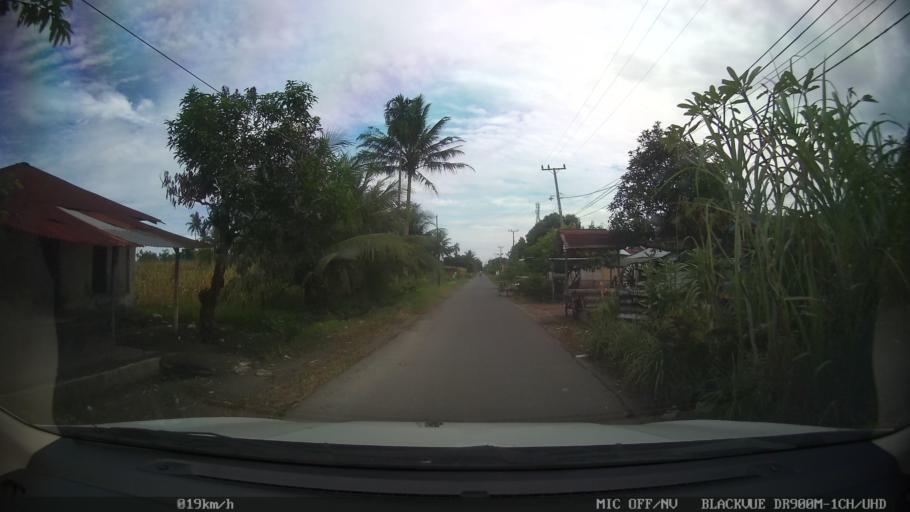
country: ID
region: North Sumatra
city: Sunggal
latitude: 3.5729
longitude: 98.5640
